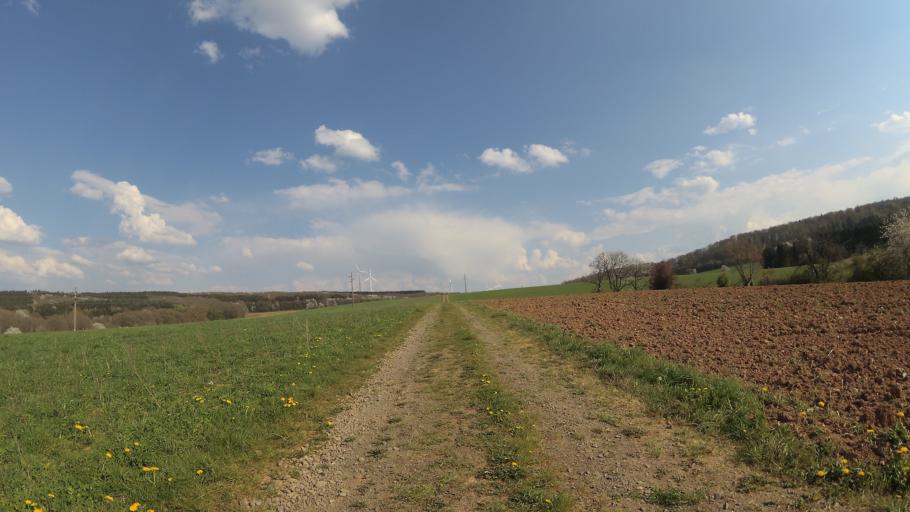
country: DE
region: Saarland
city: Sankt Wendel
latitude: 49.4481
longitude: 7.1758
